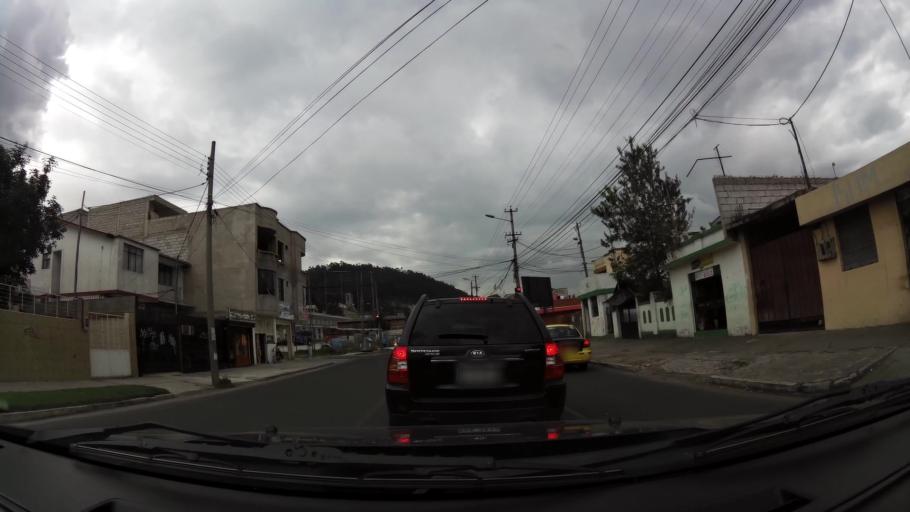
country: EC
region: Pichincha
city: Quito
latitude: -0.2406
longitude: -78.5246
